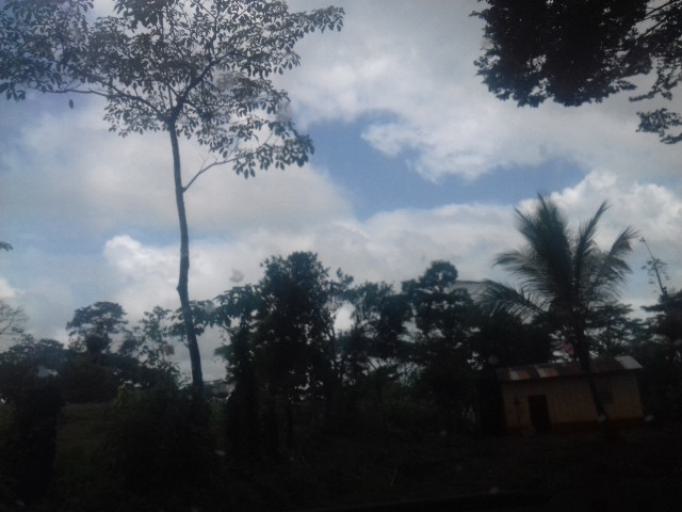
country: NI
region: Matagalpa
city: Matiguas
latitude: 12.9374
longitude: -85.3687
